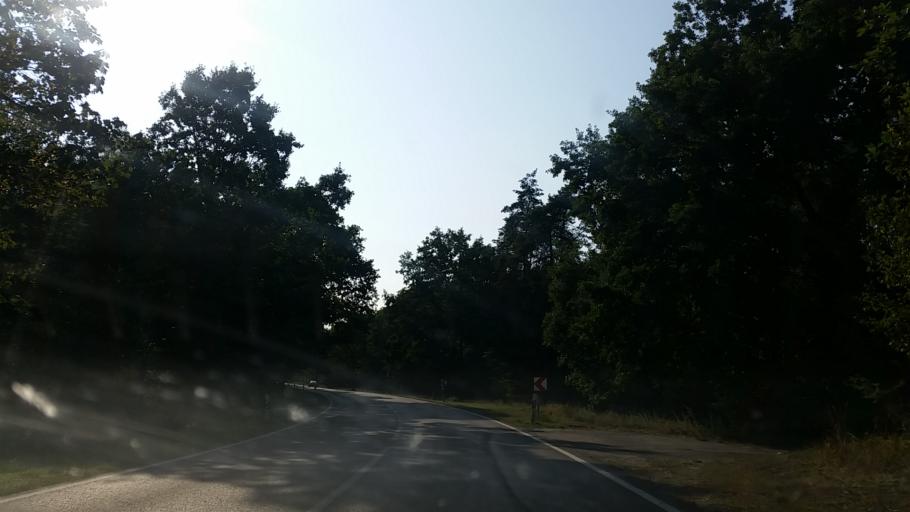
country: DE
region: Brandenburg
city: Passow
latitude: 53.1231
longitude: 14.1745
